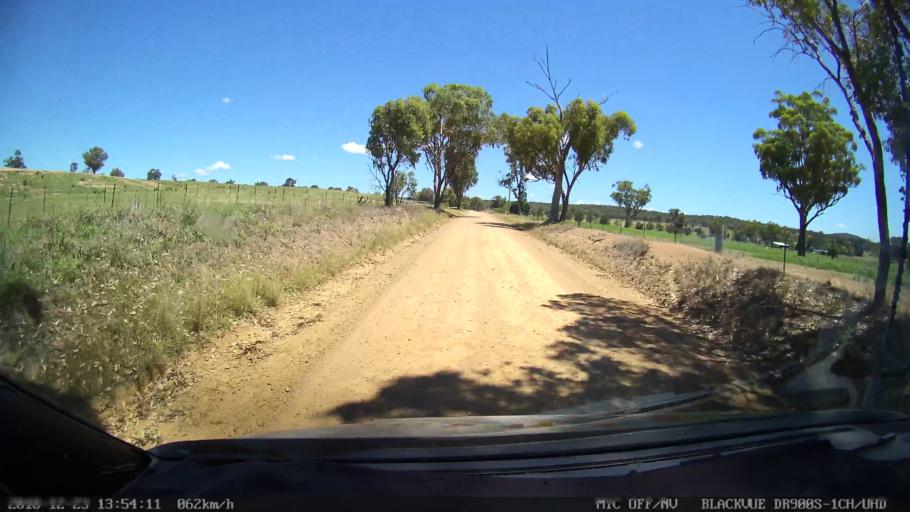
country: AU
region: New South Wales
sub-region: Tamworth Municipality
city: Manilla
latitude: -30.5587
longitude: 151.0911
